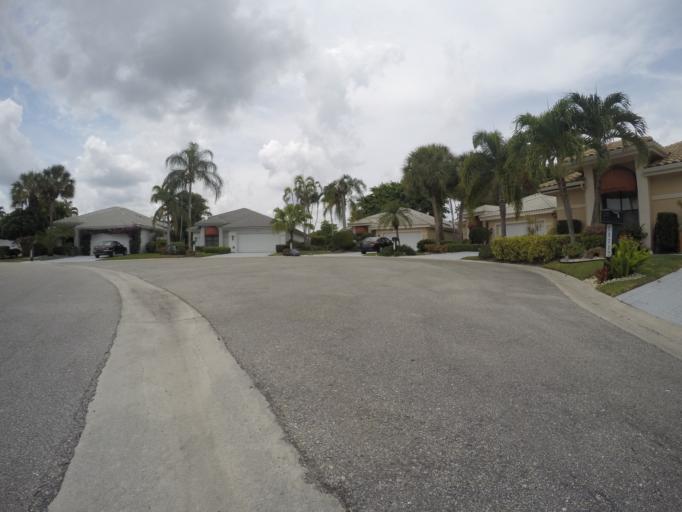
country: US
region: Florida
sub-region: Palm Beach County
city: Villages of Oriole
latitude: 26.4152
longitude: -80.2078
